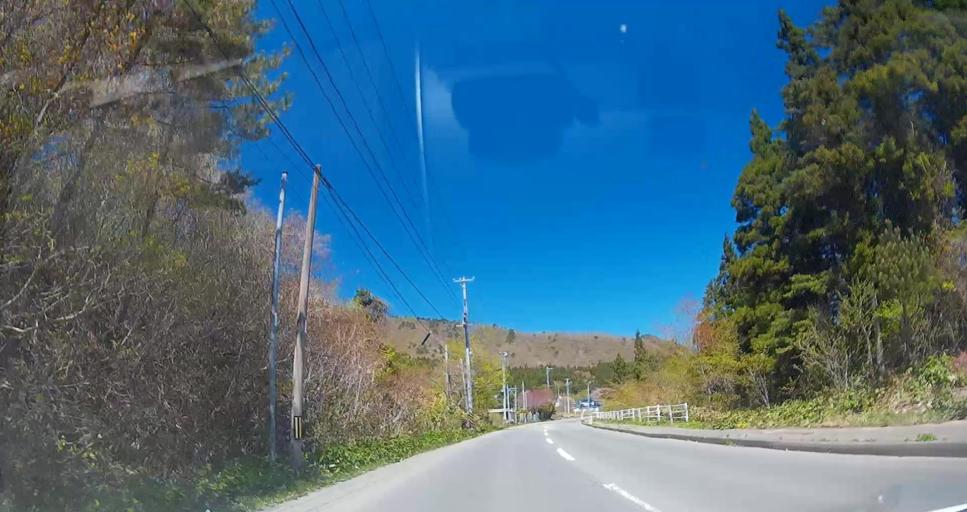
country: JP
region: Aomori
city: Mutsu
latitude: 41.1005
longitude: 141.3890
